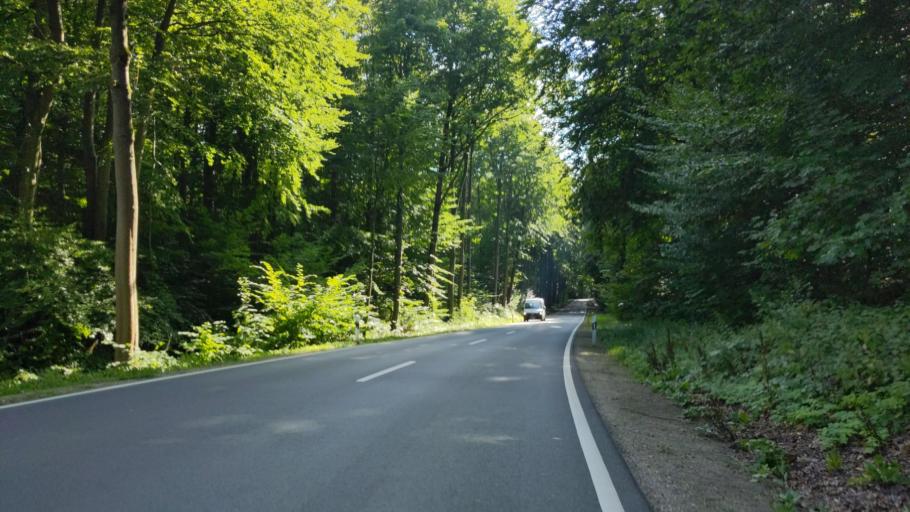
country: DE
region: Schleswig-Holstein
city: Kasseedorf
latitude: 54.1530
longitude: 10.7143
